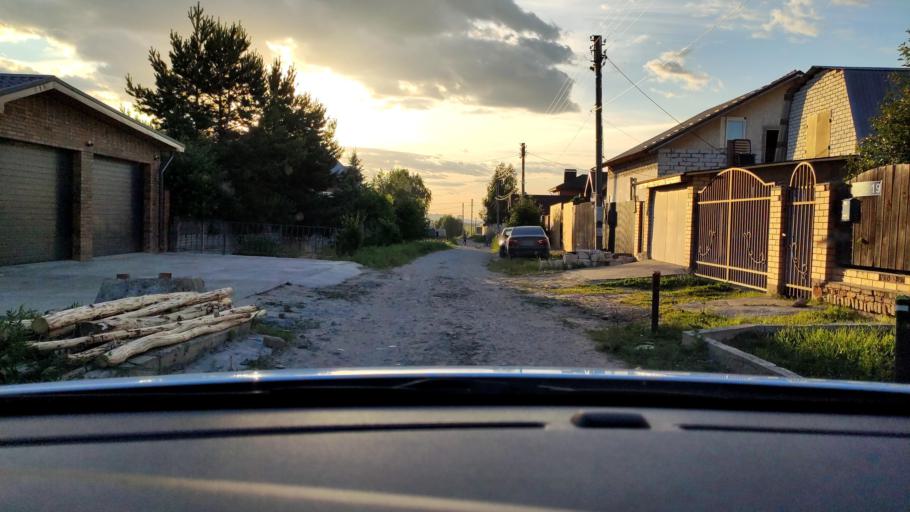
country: RU
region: Tatarstan
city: Stolbishchi
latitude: 55.7571
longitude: 49.2826
